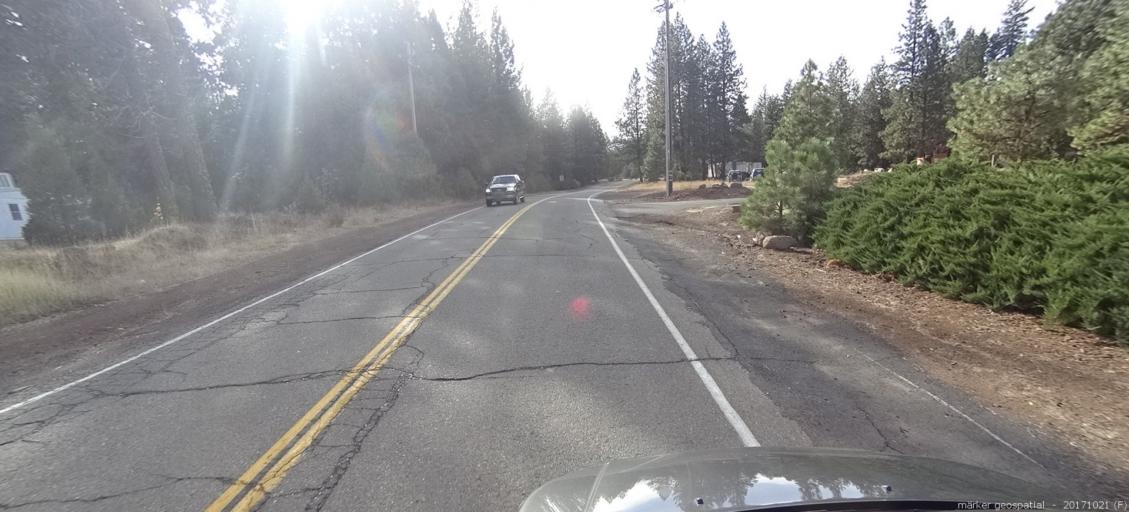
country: US
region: California
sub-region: Shasta County
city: Burney
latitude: 40.8760
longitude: -121.6766
